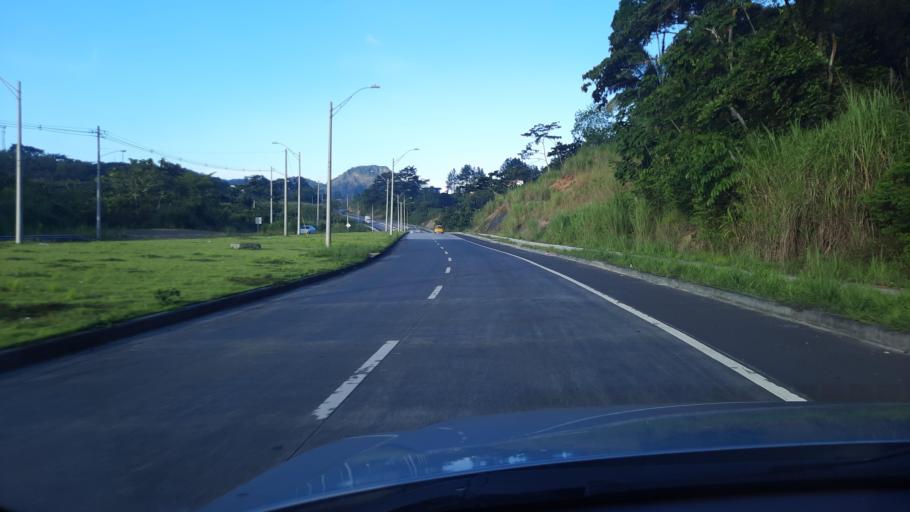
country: PA
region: Panama
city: Las Cumbres
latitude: 9.1045
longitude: -79.5279
